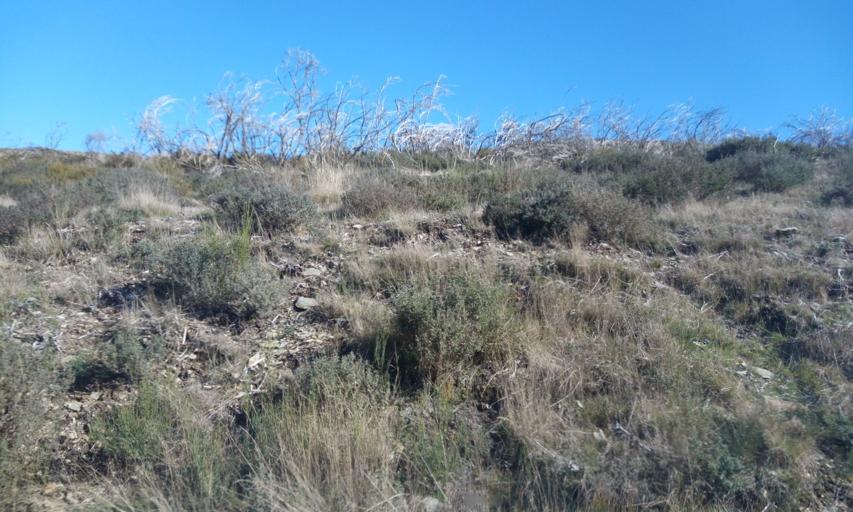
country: PT
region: Guarda
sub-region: Manteigas
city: Manteigas
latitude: 40.4527
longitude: -7.4934
